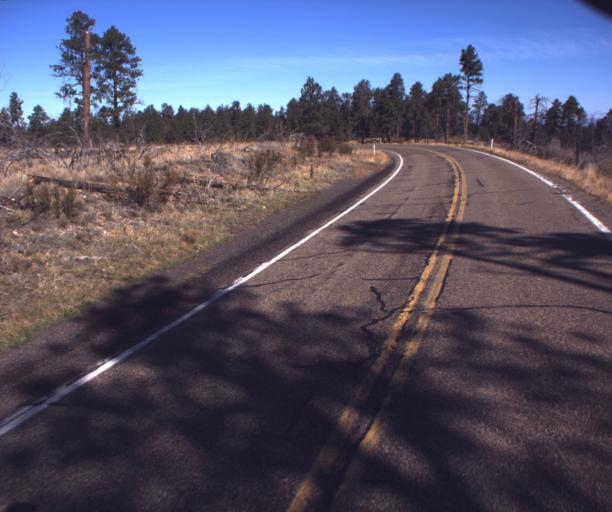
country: US
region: Arizona
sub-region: Coconino County
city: Fredonia
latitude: 36.7721
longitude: -112.2525
